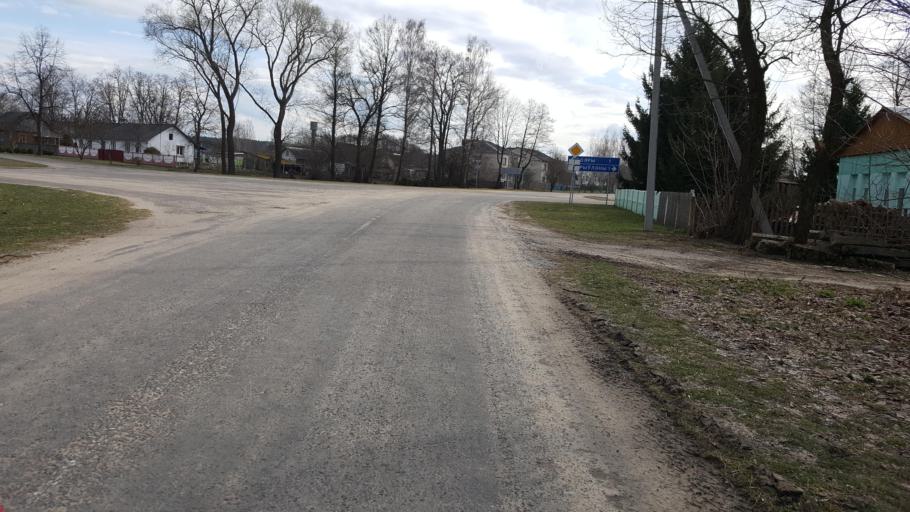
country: BY
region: Brest
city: Kamyanyets
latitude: 52.3941
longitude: 24.0029
